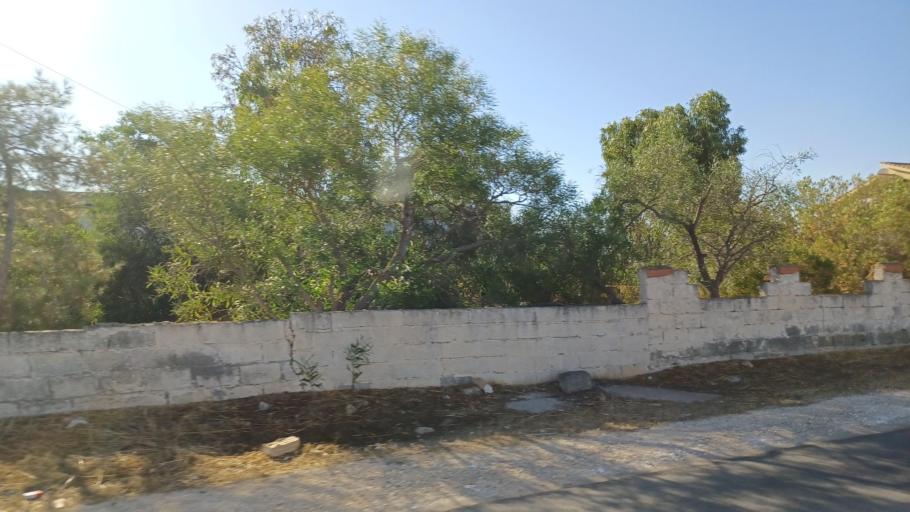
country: CY
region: Larnaka
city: Pergamos
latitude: 35.0310
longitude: 33.7053
